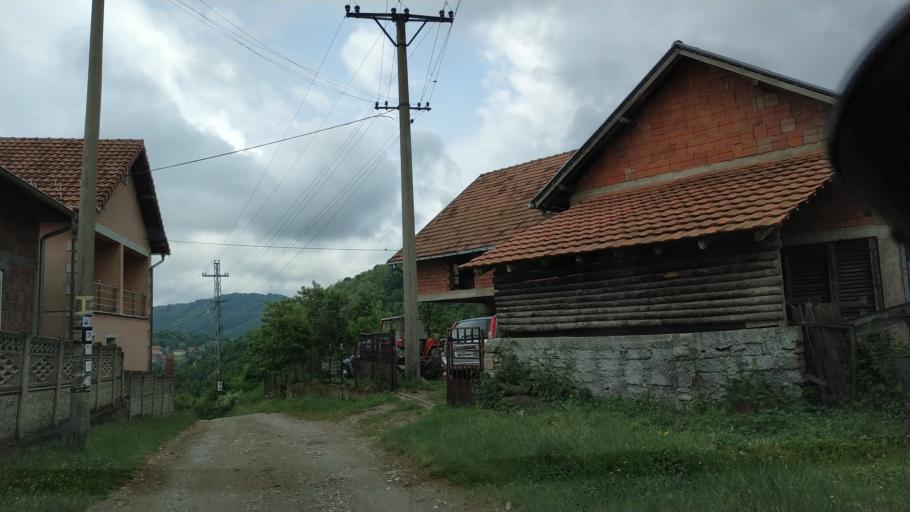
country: RS
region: Central Serbia
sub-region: Toplicki Okrug
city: Prokuplje
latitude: 43.4011
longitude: 21.5475
